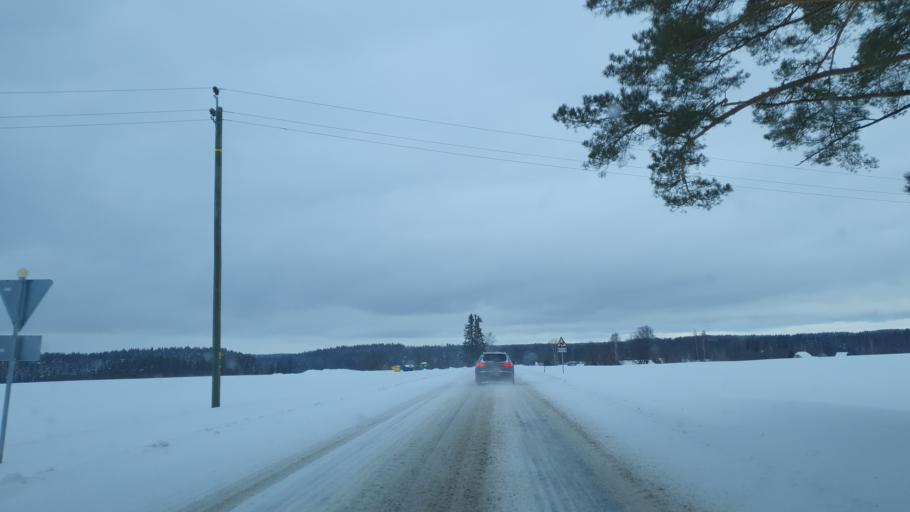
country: EE
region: Polvamaa
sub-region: Polva linn
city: Polva
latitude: 58.0991
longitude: 27.0937
